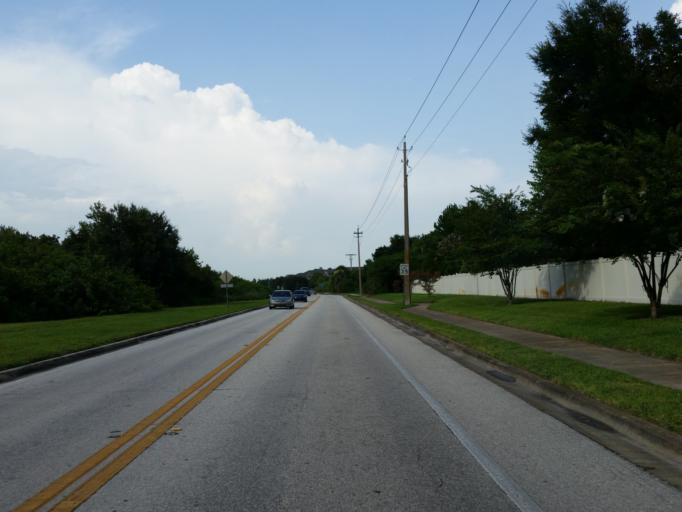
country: US
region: Florida
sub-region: Hillsborough County
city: Progress Village
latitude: 27.9096
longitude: -82.3284
